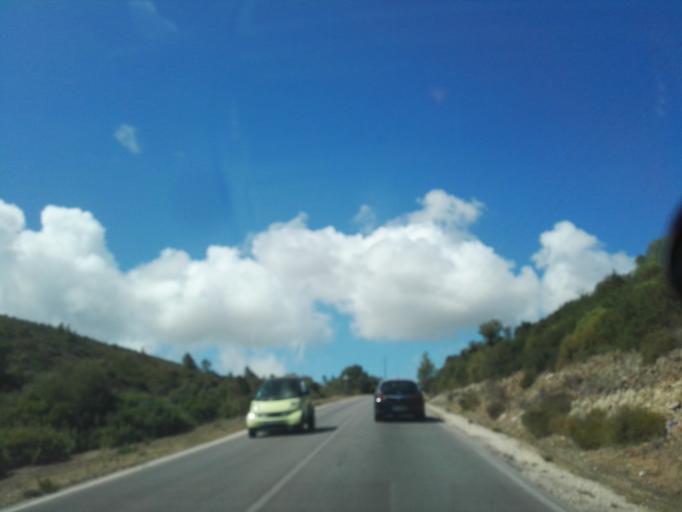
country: PT
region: Setubal
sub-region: Sesimbra
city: Sesimbra
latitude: 38.4439
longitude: -9.0862
